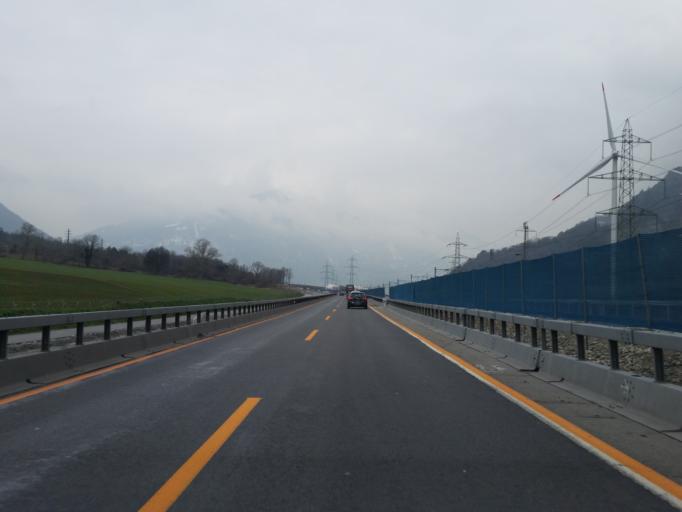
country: CH
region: Grisons
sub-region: Landquart District
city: Trimmis
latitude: 46.8977
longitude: 9.5439
